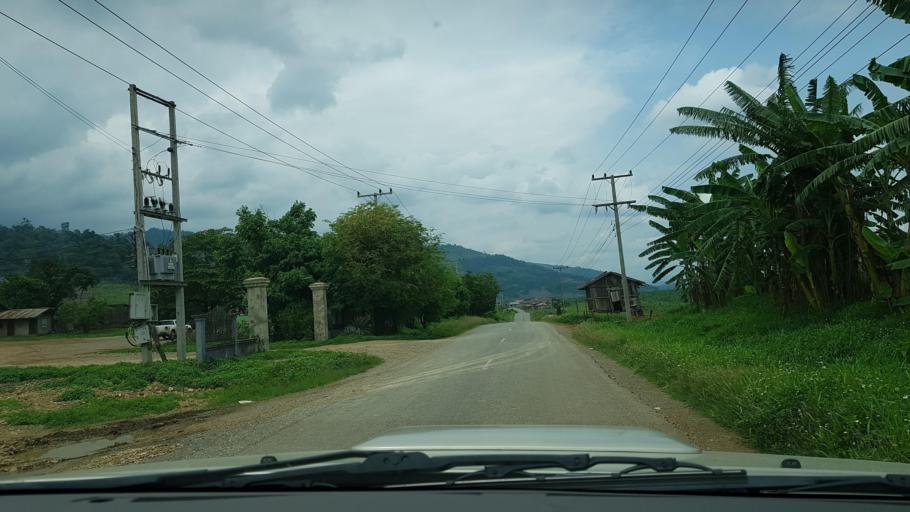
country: TH
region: Nan
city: Chaloem Phra Kiat
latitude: 19.9789
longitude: 101.2723
